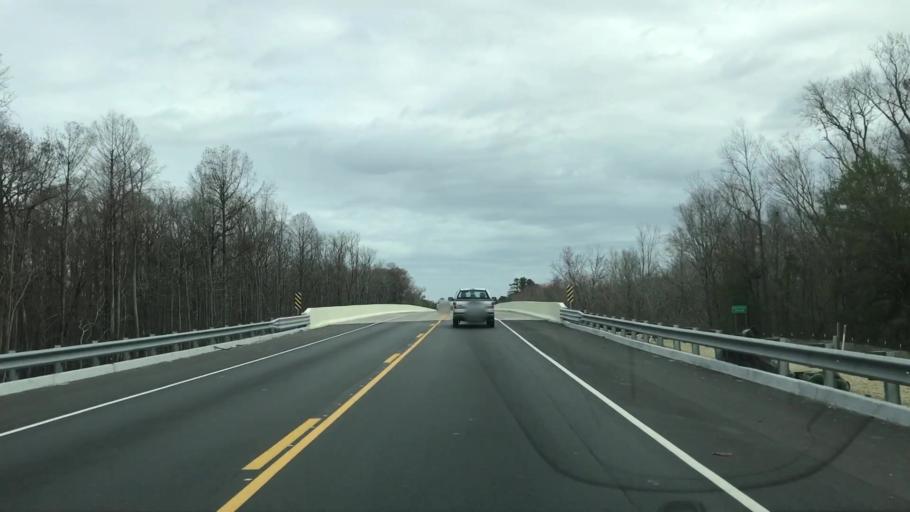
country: US
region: South Carolina
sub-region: Horry County
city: Socastee
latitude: 33.6664
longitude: -79.1463
